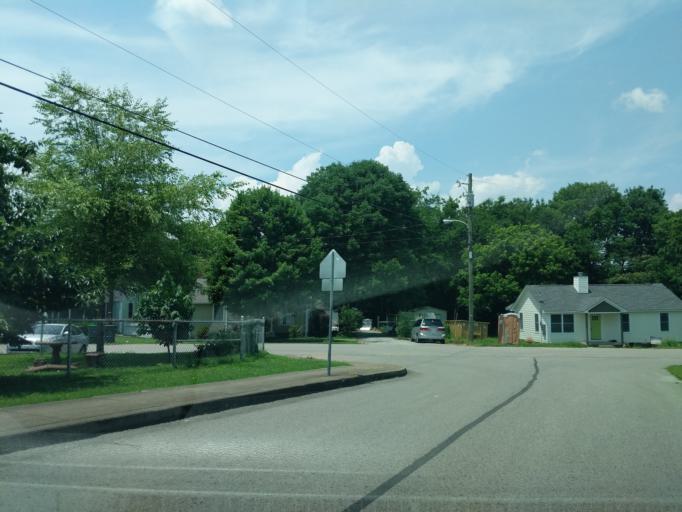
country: US
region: Tennessee
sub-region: Davidson County
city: Lakewood
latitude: 36.2268
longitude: -86.6342
